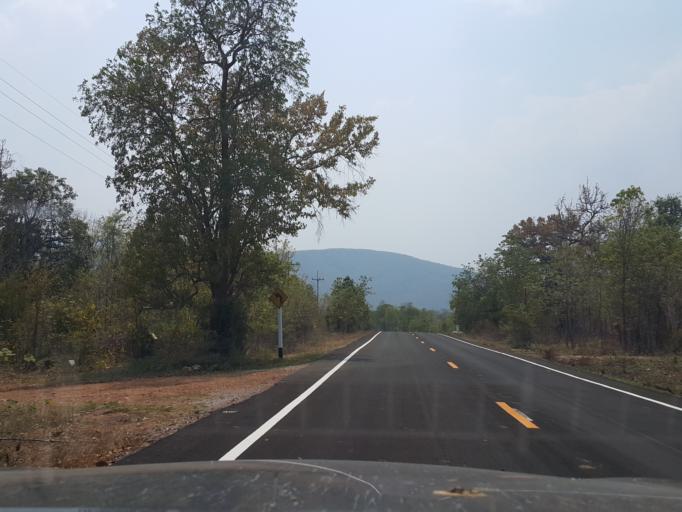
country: TH
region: Lampang
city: Mae Phrik
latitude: 17.4891
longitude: 99.0947
